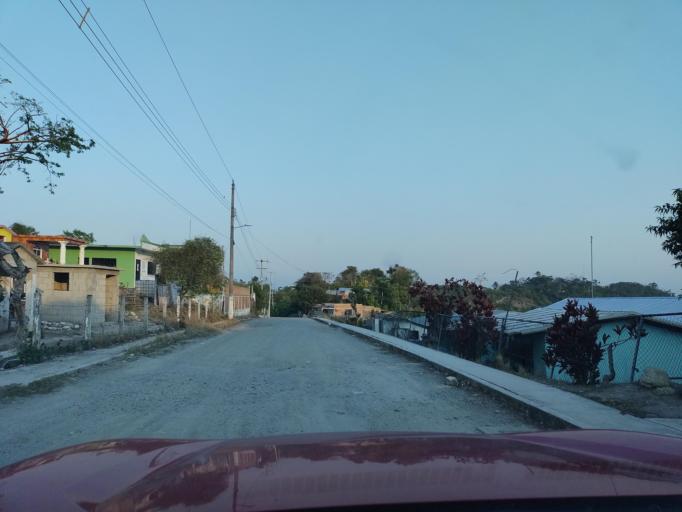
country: MX
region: Veracruz
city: Agua Dulce
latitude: 20.4043
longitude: -97.2884
